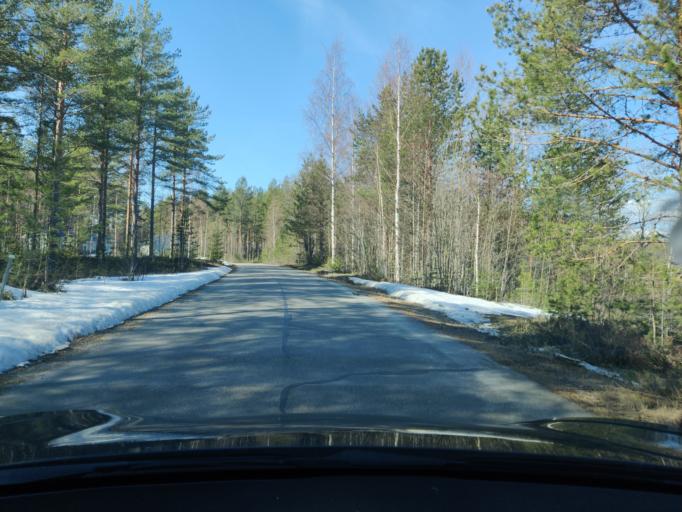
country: FI
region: Northern Savo
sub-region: Kuopio
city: Vehmersalmi
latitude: 62.7733
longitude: 27.9826
